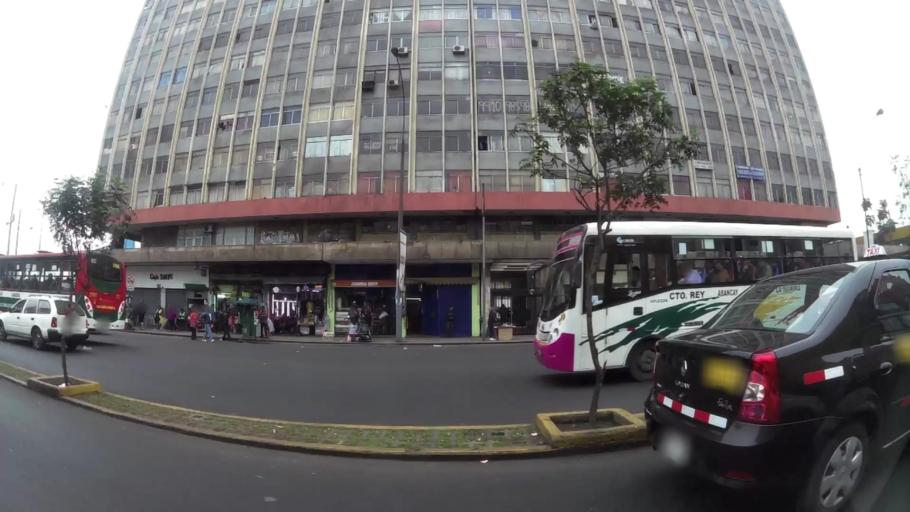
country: PE
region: Lima
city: Lima
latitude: -12.0585
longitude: -77.0299
